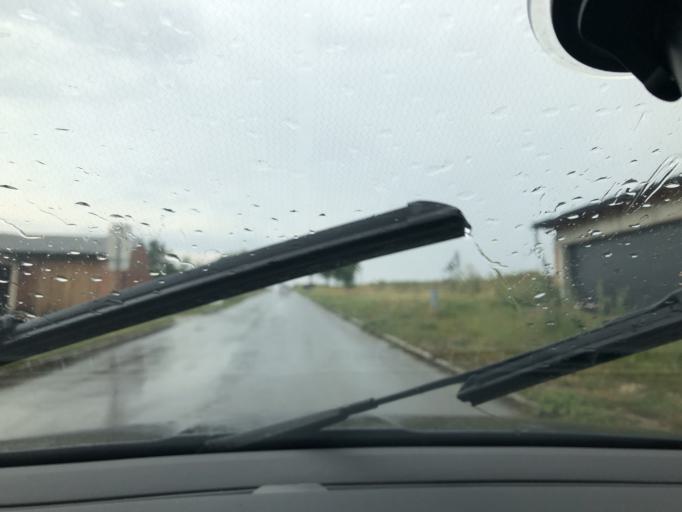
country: AT
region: Lower Austria
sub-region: Politischer Bezirk Ganserndorf
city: Auersthal
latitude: 48.3741
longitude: 16.6422
